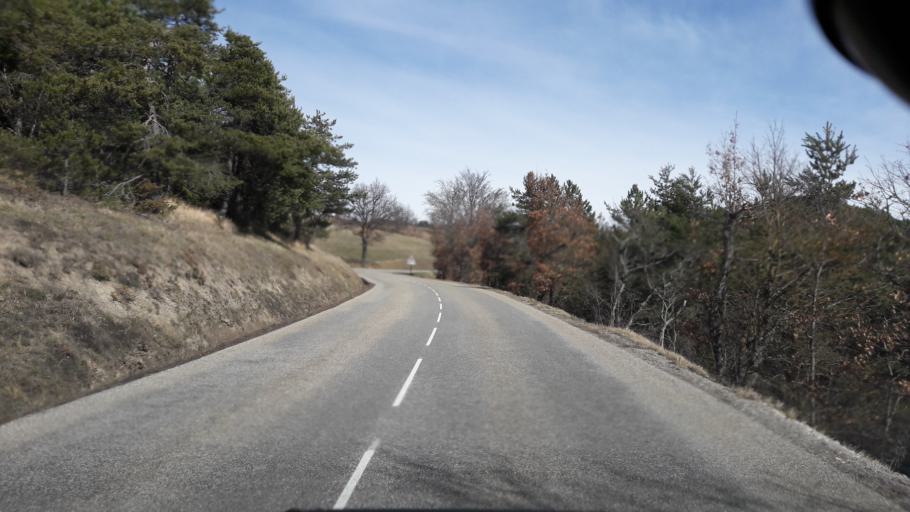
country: FR
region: Rhone-Alpes
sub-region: Departement de l'Isere
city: Mens
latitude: 44.8358
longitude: 5.7769
